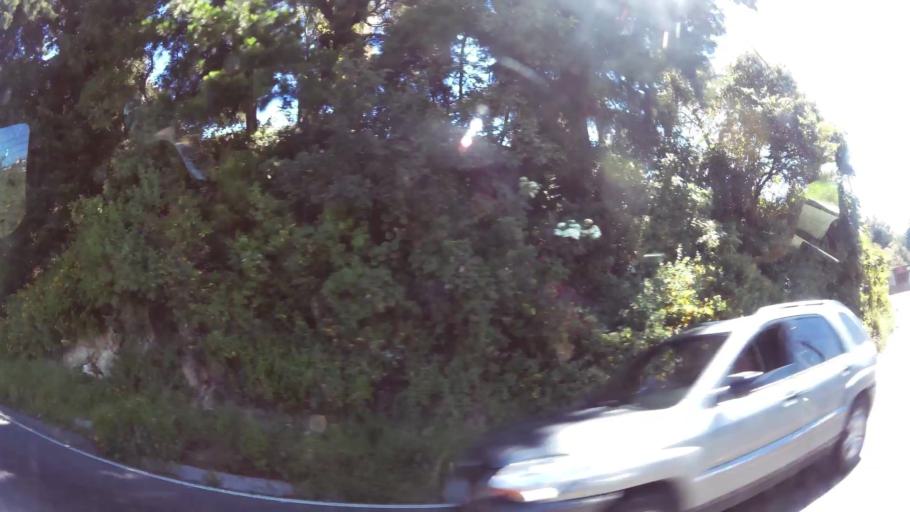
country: GT
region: Solola
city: Solola
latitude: 14.7641
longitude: -91.1781
